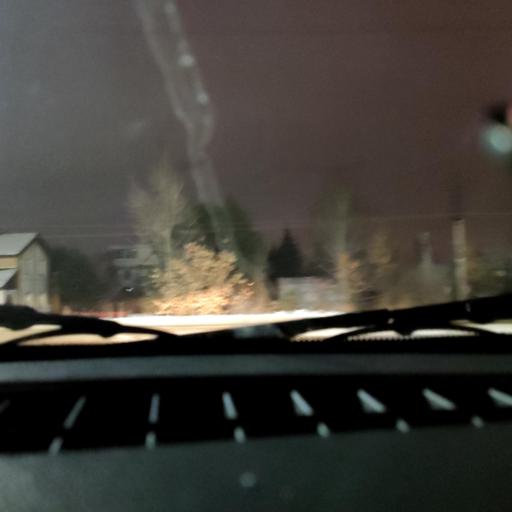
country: RU
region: Bashkortostan
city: Ufa
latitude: 54.6570
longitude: 56.0606
